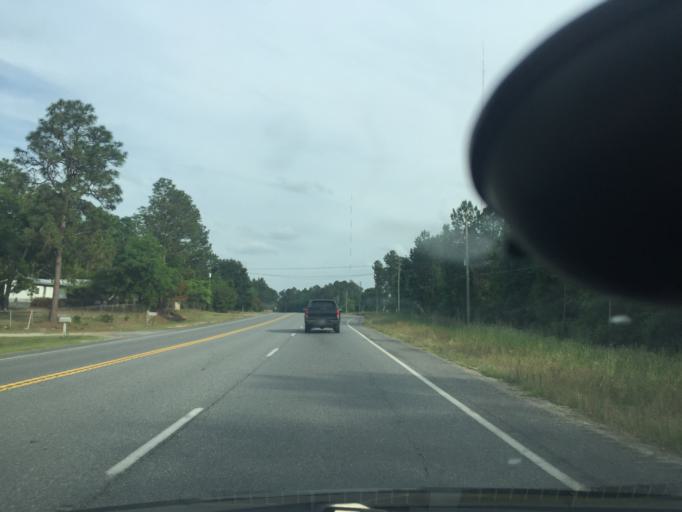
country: US
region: Georgia
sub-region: Chatham County
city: Bloomingdale
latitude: 32.0623
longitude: -81.3543
